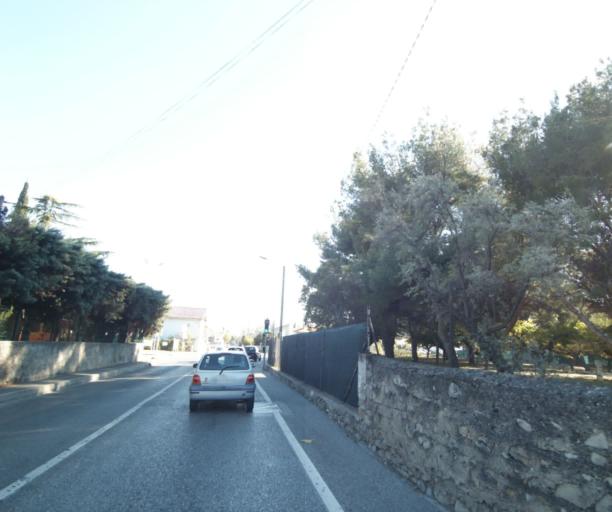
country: FR
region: Provence-Alpes-Cote d'Azur
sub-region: Departement des Bouches-du-Rhone
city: La Ciotat
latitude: 43.1863
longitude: 5.6072
